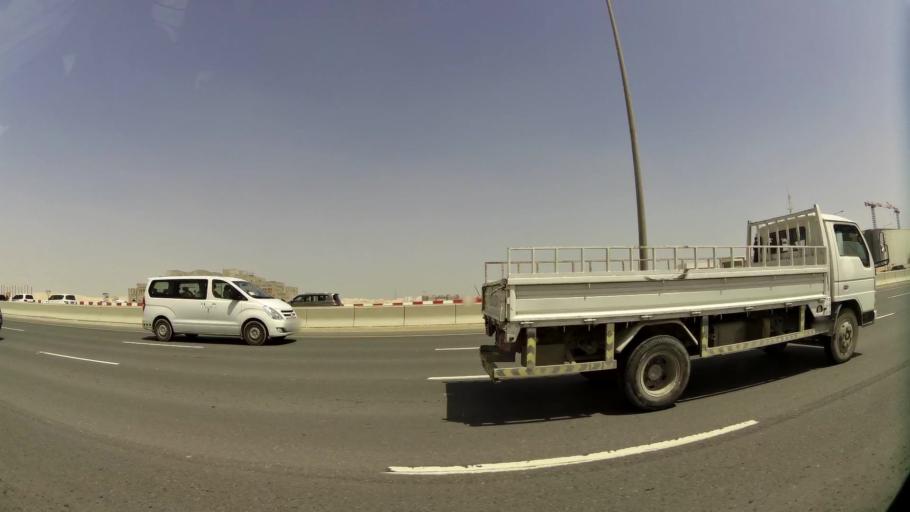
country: QA
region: Baladiyat ar Rayyan
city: Ar Rayyan
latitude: 25.3552
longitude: 51.4524
